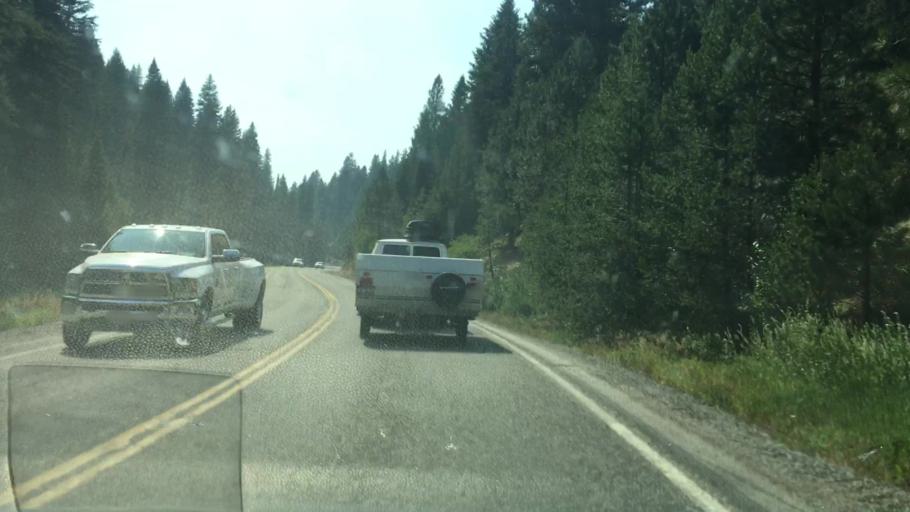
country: US
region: Idaho
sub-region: Valley County
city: Cascade
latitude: 44.3356
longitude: -116.0431
